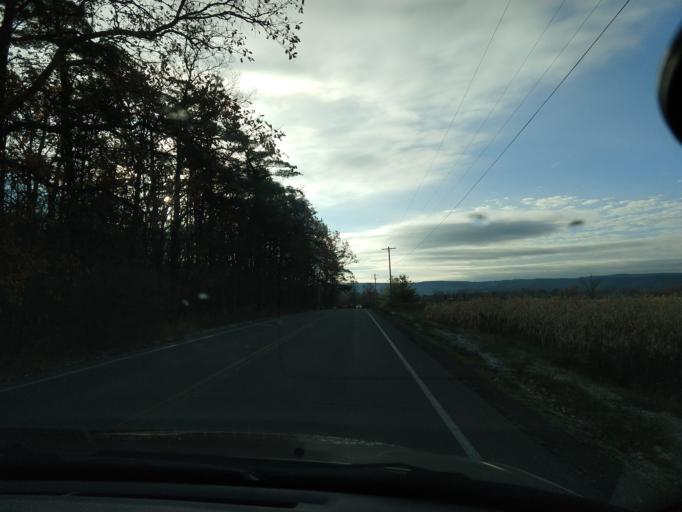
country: US
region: New York
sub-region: Tompkins County
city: Northeast Ithaca
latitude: 42.4664
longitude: -76.4473
